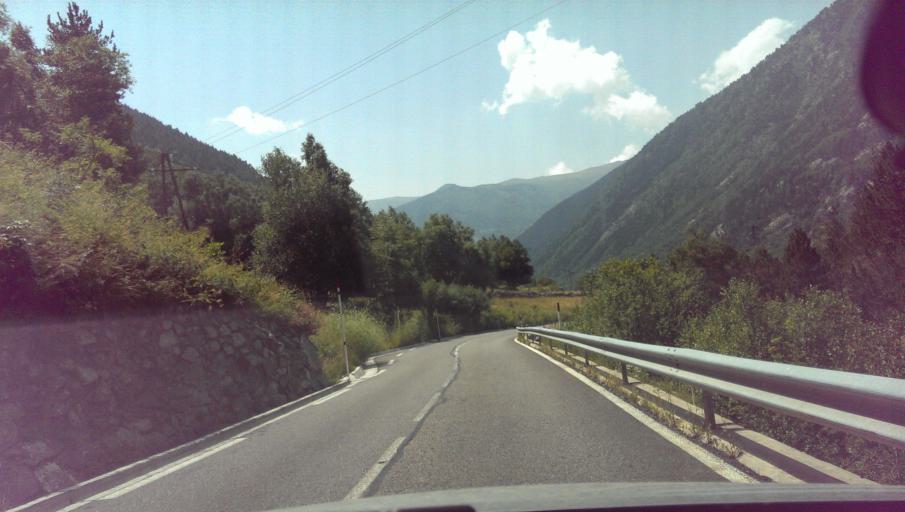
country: AD
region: Encamp
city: Pas de la Casa
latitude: 42.5406
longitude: 1.8276
